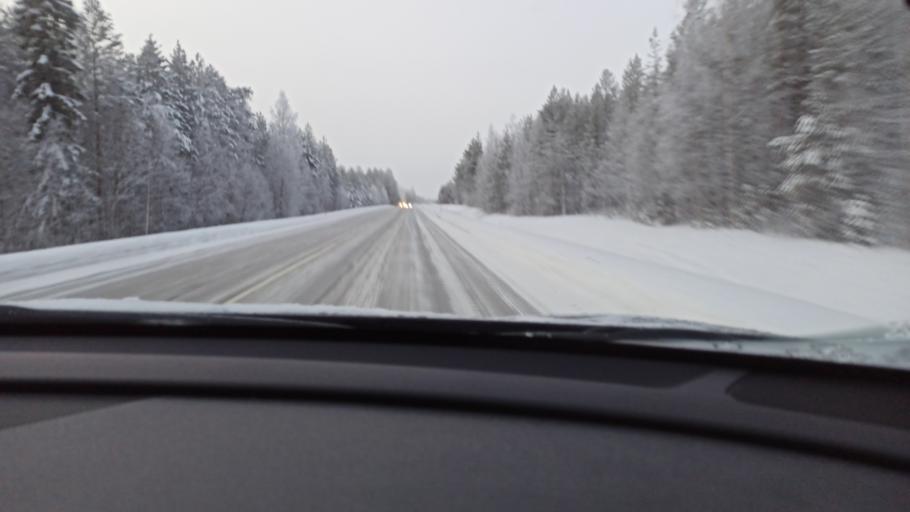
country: FI
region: Lapland
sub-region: Pohjois-Lappi
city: Sodankylae
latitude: 66.9371
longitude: 26.2755
